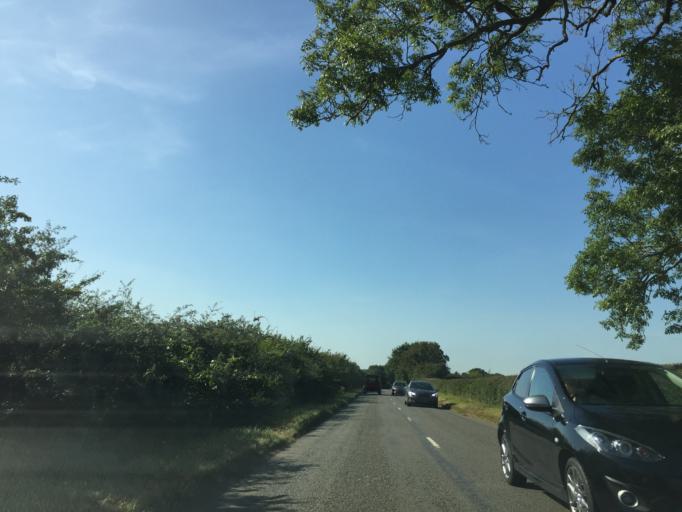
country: GB
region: England
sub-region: Leicestershire
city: Queniborough
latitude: 52.7008
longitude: -1.0260
